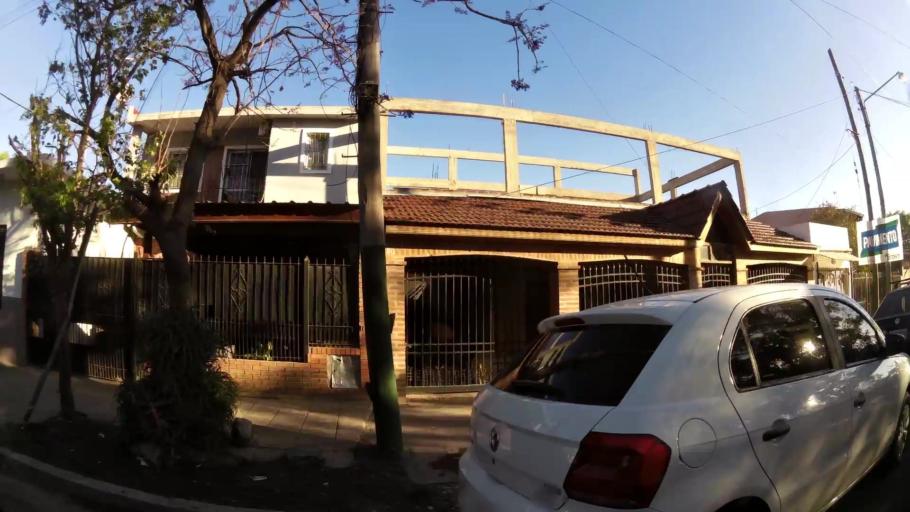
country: AR
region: Buenos Aires
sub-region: Partido de Almirante Brown
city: Adrogue
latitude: -34.7710
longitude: -58.3379
